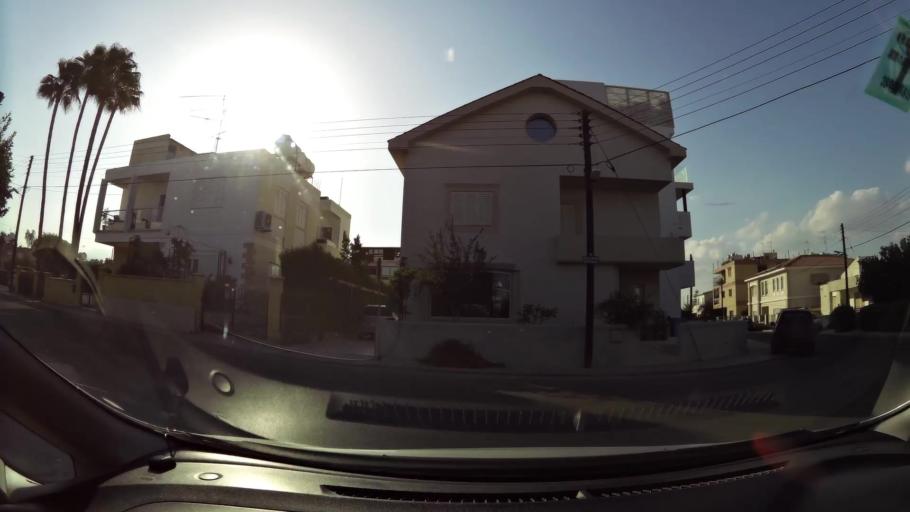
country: CY
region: Lefkosia
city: Nicosia
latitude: 35.1761
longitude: 33.3330
